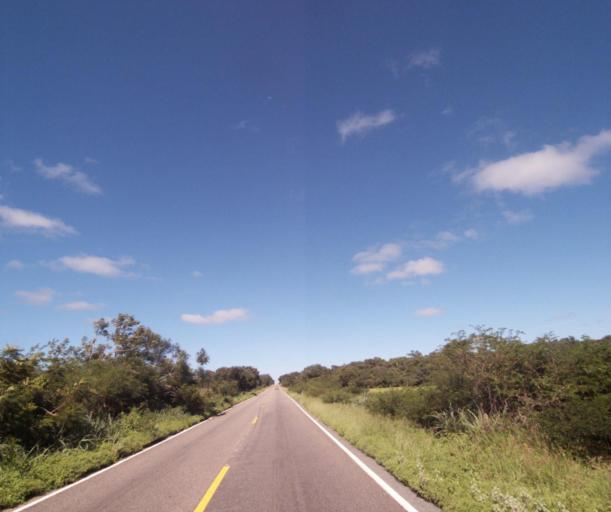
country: BR
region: Bahia
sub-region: Palmas De Monte Alto
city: Palmas de Monte Alto
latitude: -14.2425
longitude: -43.0755
